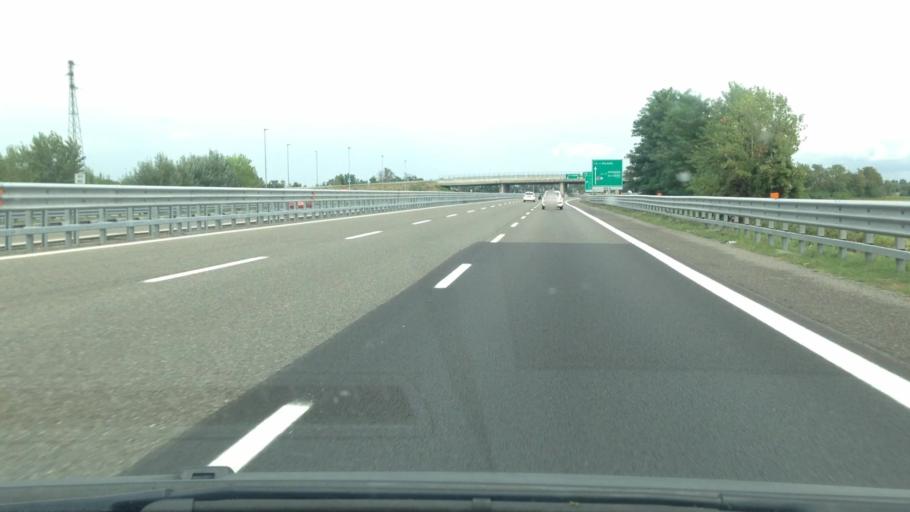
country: IT
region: Piedmont
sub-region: Provincia di Alessandria
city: Tortona
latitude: 44.9171
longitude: 8.8446
